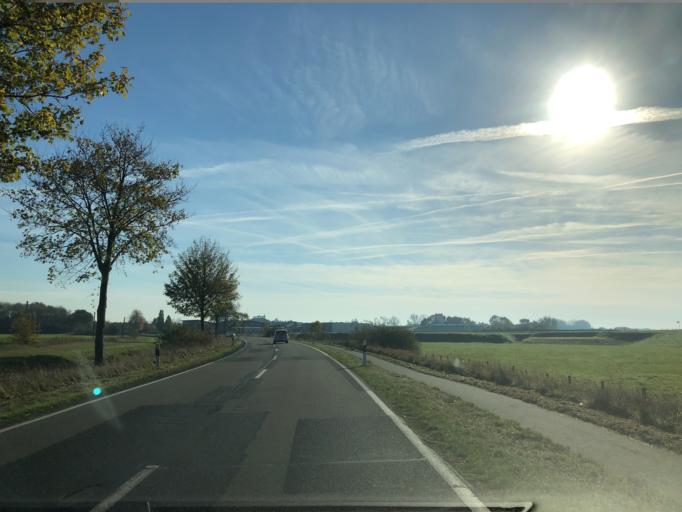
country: DE
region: Lower Saxony
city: Rhede
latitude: 53.0525
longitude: 7.3172
